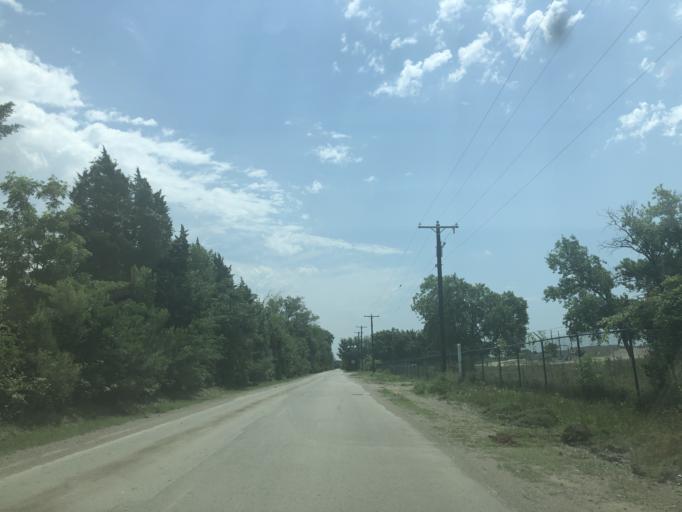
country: US
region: Texas
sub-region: Dallas County
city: Irving
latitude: 32.7866
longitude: -96.9436
